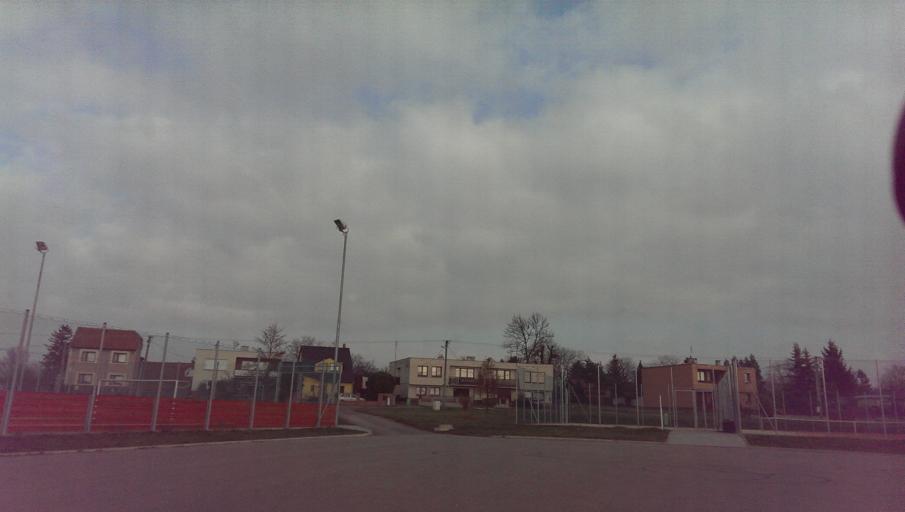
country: CZ
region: Zlin
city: Tlumacov
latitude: 49.2497
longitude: 17.4936
